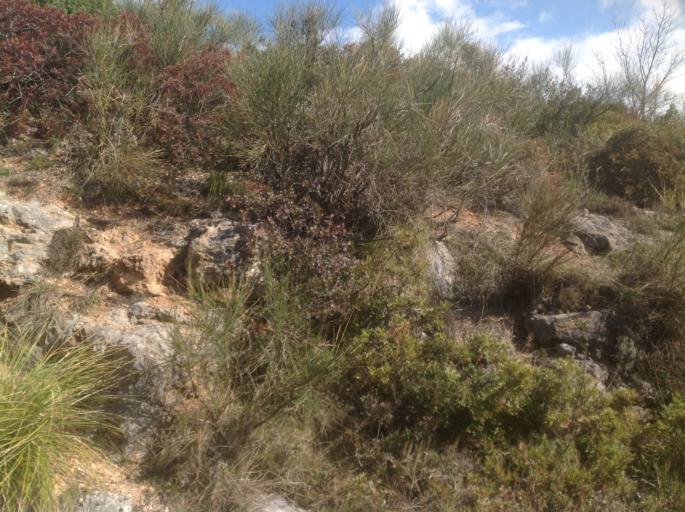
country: IT
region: Calabria
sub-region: Provincia di Cosenza
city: Civita
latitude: 39.8246
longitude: 16.3087
